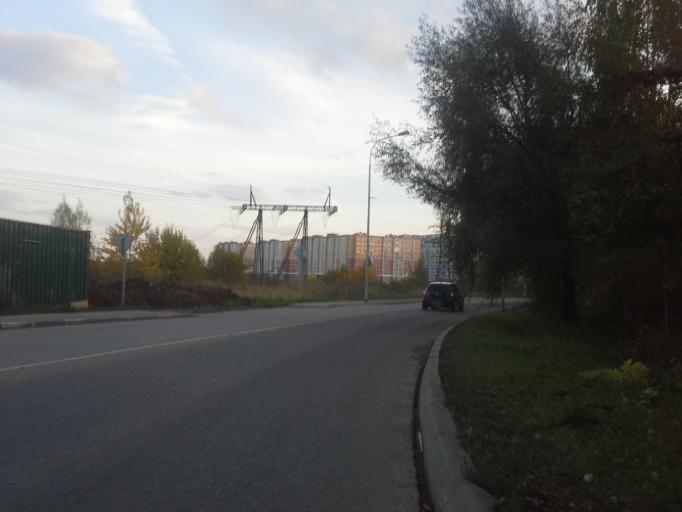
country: RU
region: Moskovskaya
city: Kommunarka
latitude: 55.5787
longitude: 37.4835
